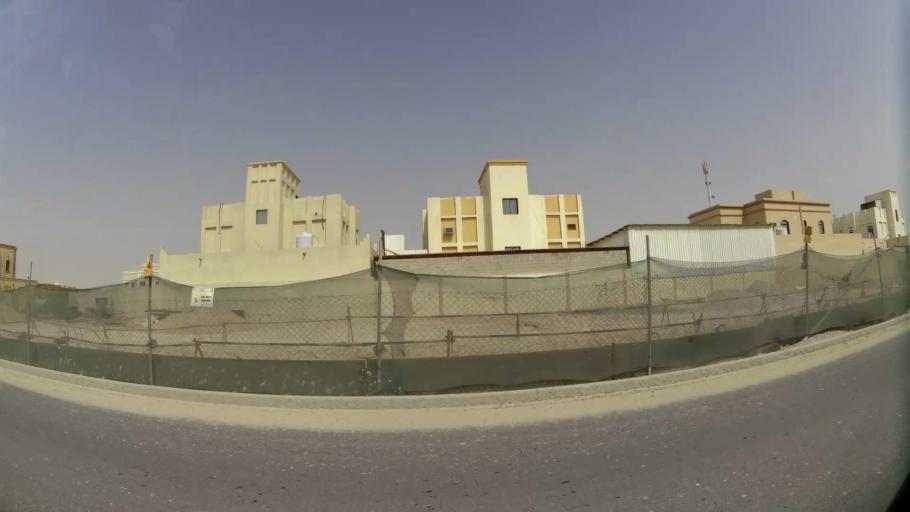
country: QA
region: Baladiyat ar Rayyan
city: Ar Rayyan
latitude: 25.2471
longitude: 51.3621
